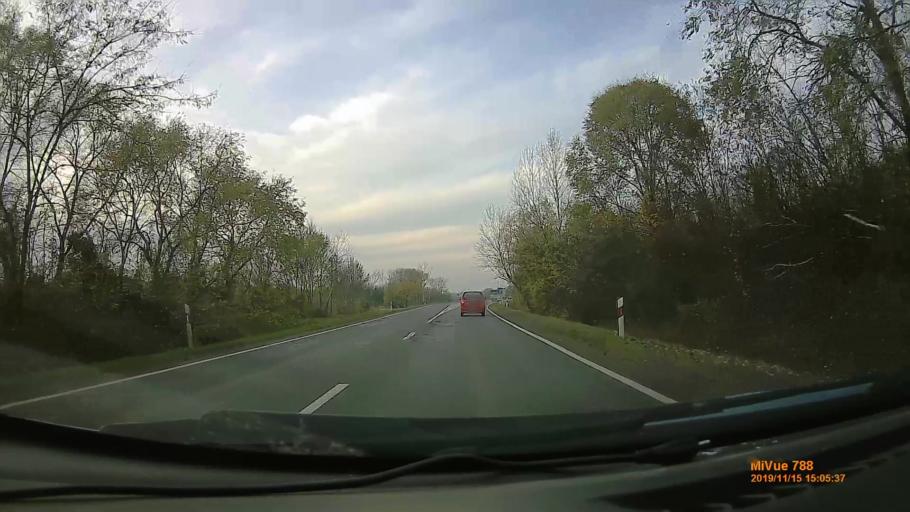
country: HU
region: Bekes
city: Gyula
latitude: 46.6359
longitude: 21.2529
